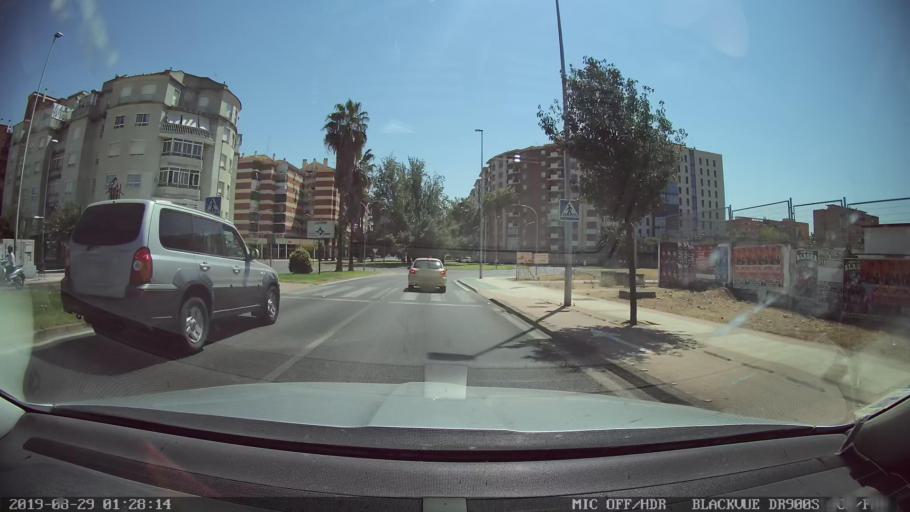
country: ES
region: Extremadura
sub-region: Provincia de Badajoz
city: Badajoz
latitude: 38.8726
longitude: -6.9905
